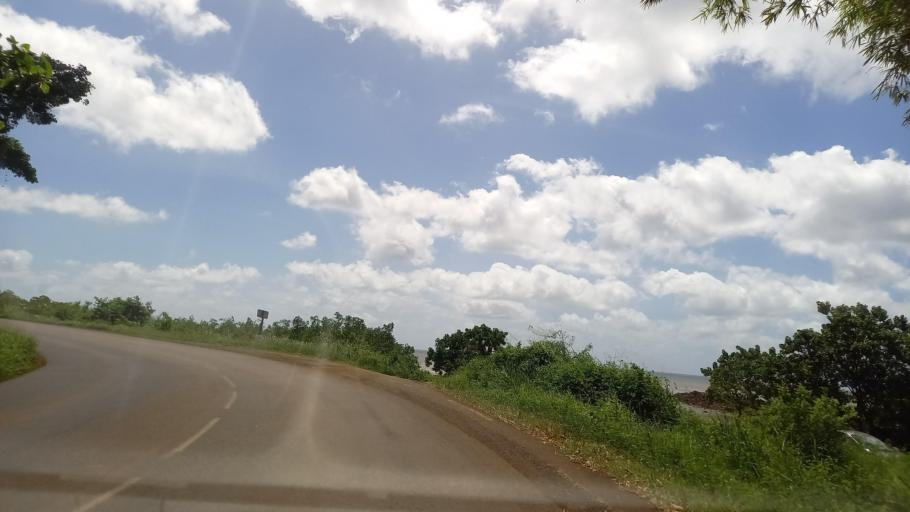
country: YT
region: Bandraboua
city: Bandraboua
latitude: -12.7220
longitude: 45.1302
